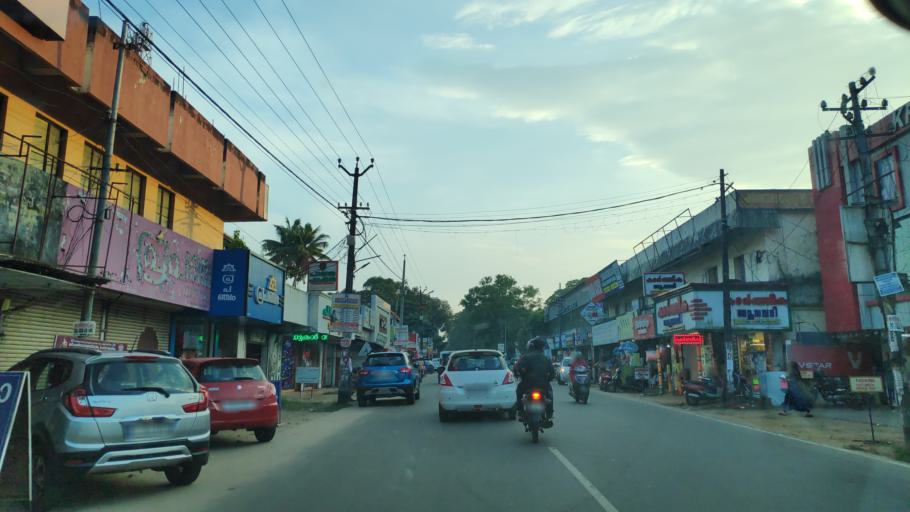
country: IN
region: Kerala
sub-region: Alappuzha
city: Shertallai
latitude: 9.6818
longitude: 76.3454
